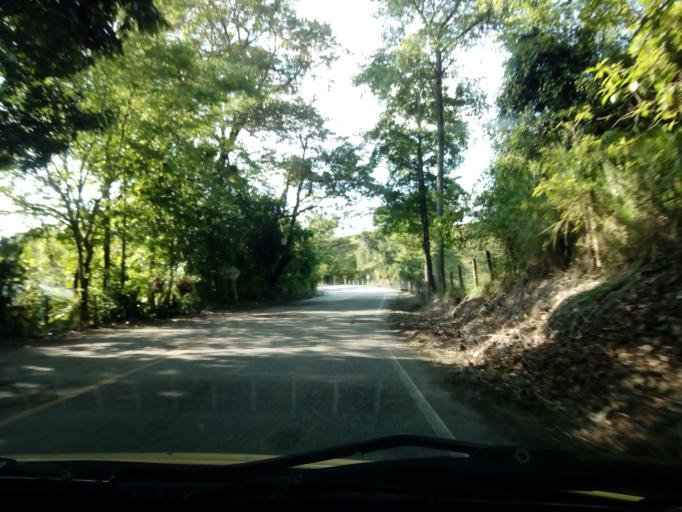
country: CO
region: Boyaca
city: Puerto Boyaca
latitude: 5.9360
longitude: -74.5421
